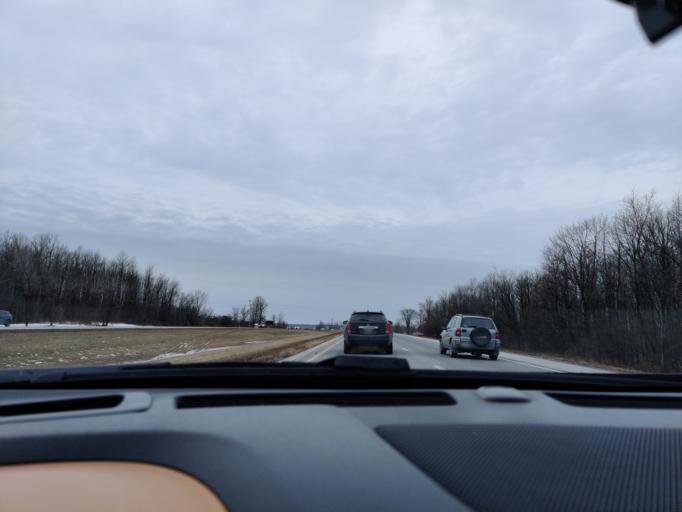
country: US
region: New York
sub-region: St. Lawrence County
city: Norfolk
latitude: 44.9053
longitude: -75.2264
